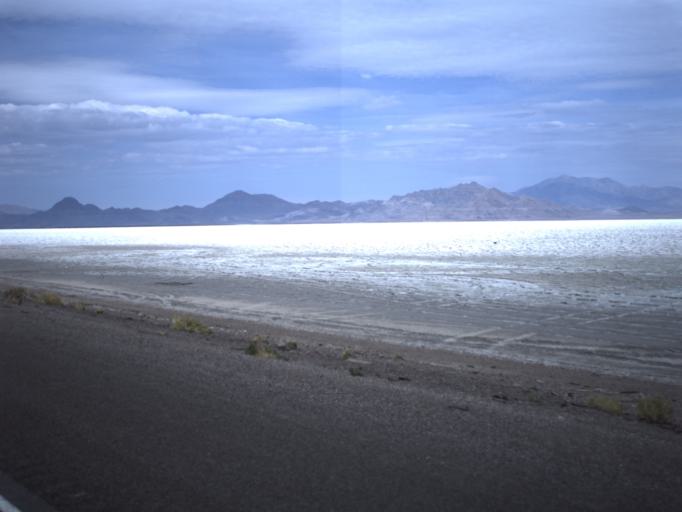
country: US
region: Utah
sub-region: Tooele County
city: Wendover
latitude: 40.7382
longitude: -113.7916
